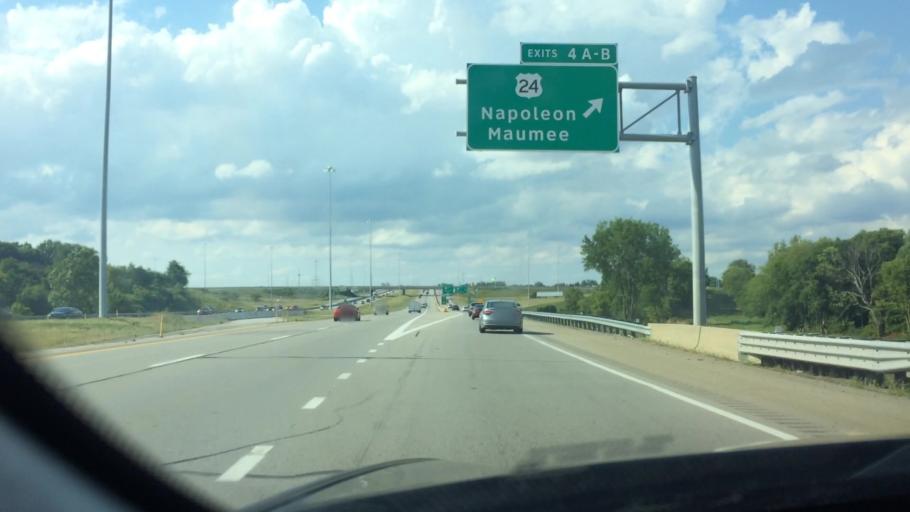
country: US
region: Ohio
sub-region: Lucas County
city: Maumee
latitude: 41.5476
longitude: -83.6835
